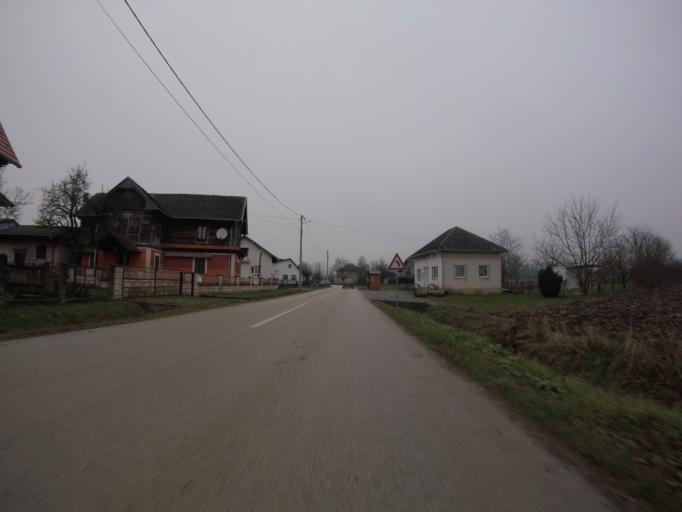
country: HR
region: Sisacko-Moslavacka
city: Lekenik
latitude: 45.6633
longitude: 16.2516
